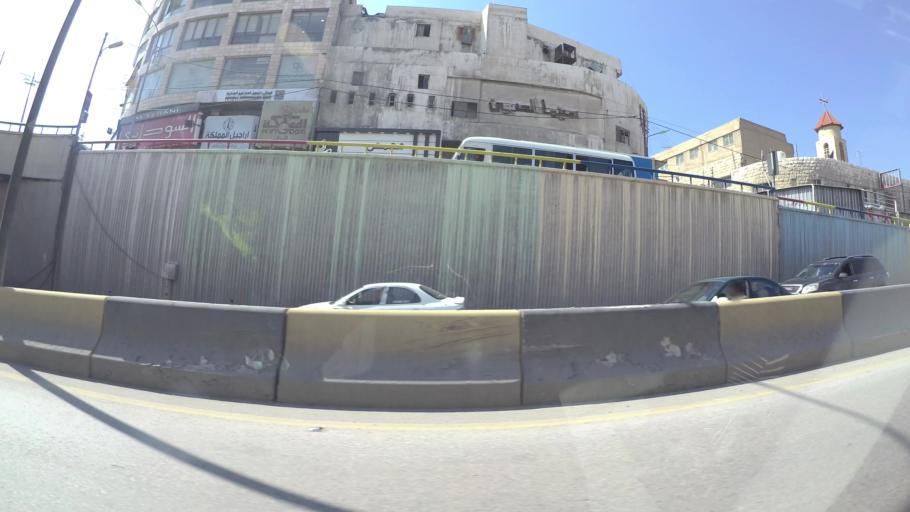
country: JO
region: Zarqa
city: Zarqa
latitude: 32.0614
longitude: 36.0943
